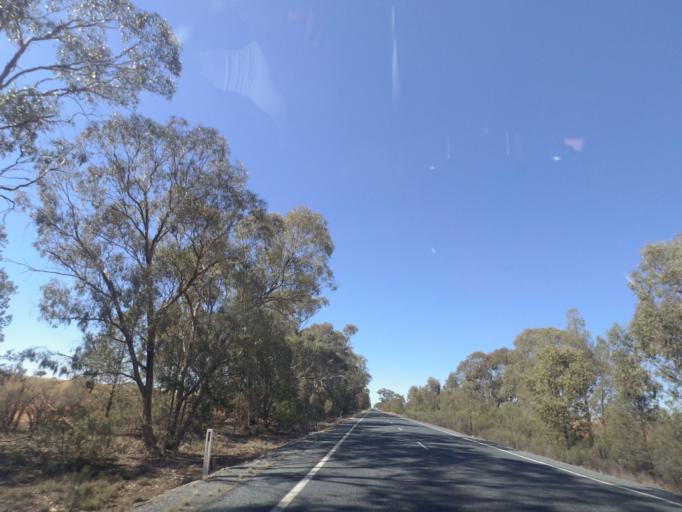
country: AU
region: New South Wales
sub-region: Bland
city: West Wyalong
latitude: -34.1510
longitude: 147.1185
